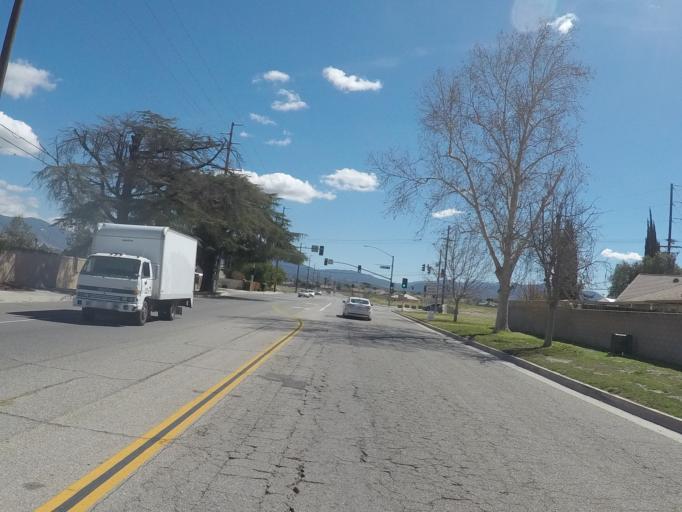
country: US
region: California
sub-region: Riverside County
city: East Hemet
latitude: 33.7662
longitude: -116.9243
